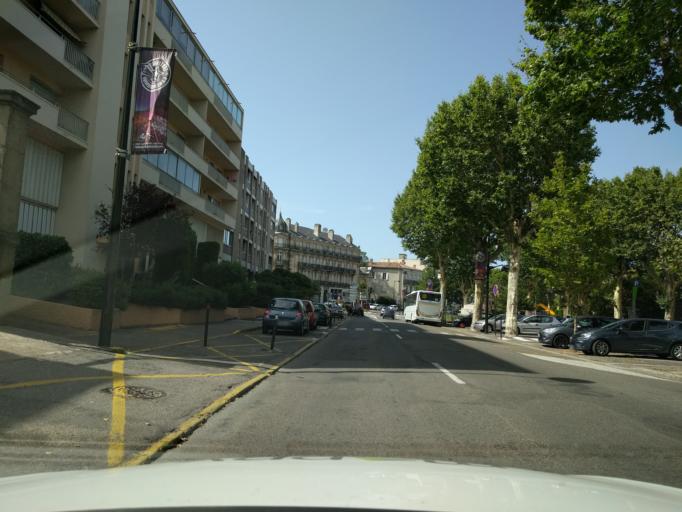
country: FR
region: Languedoc-Roussillon
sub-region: Departement de l'Aude
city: Carcassonne
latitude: 43.2118
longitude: 2.3465
